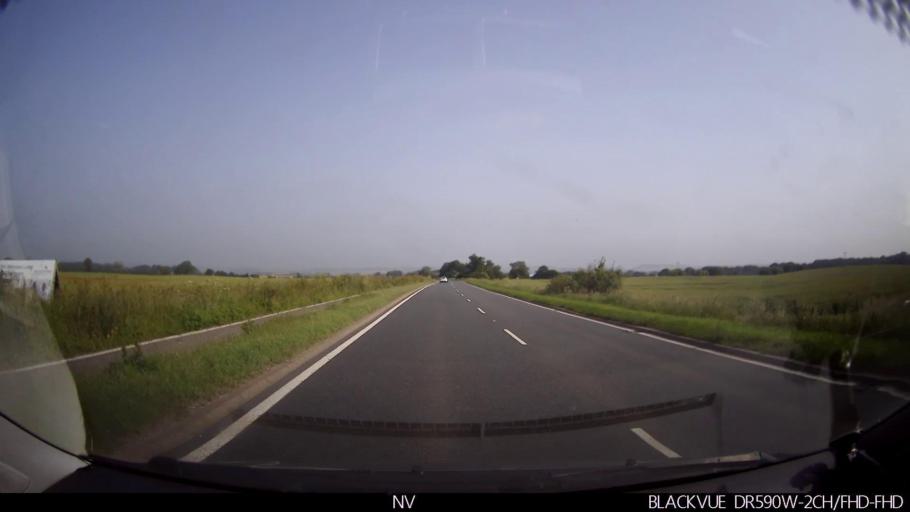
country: GB
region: England
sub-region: North Yorkshire
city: East Ayton
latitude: 54.2079
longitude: -0.4353
